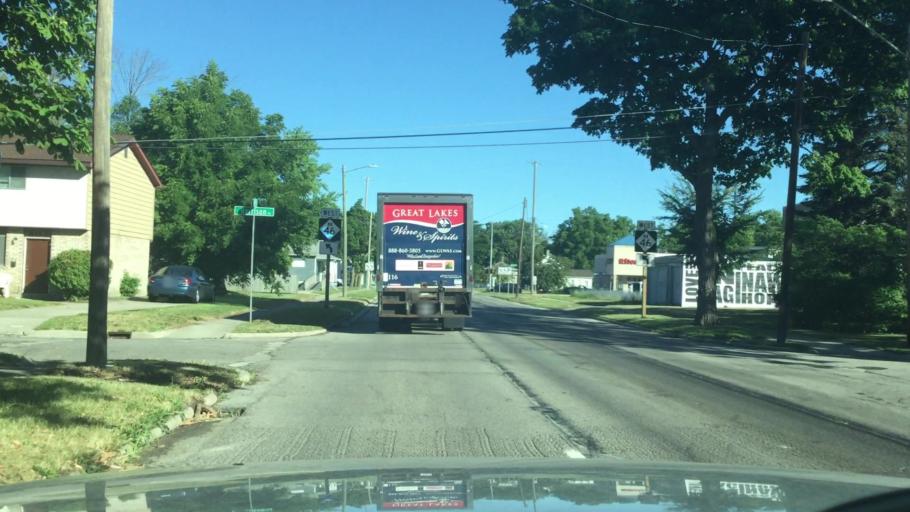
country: US
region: Michigan
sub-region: Saginaw County
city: Saginaw
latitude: 43.4141
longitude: -83.9716
